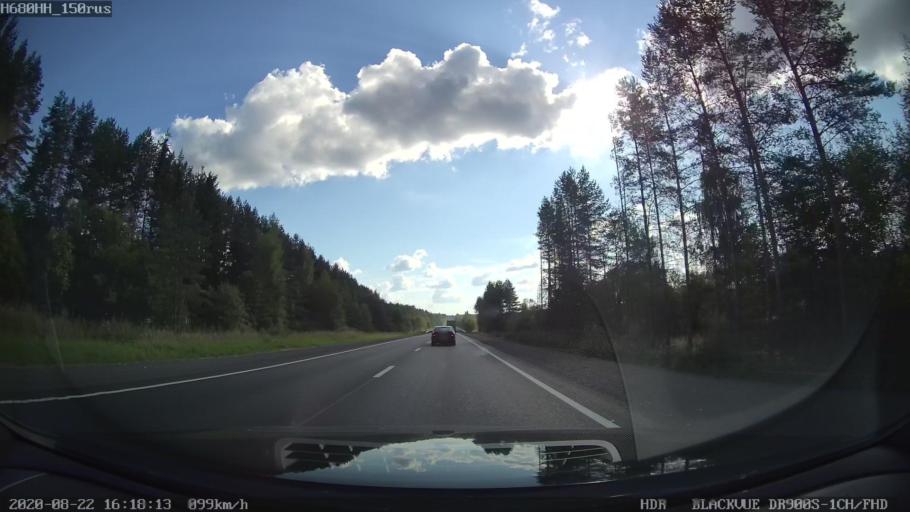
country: RU
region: Tverskaya
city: Rameshki
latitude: 57.4192
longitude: 36.1451
